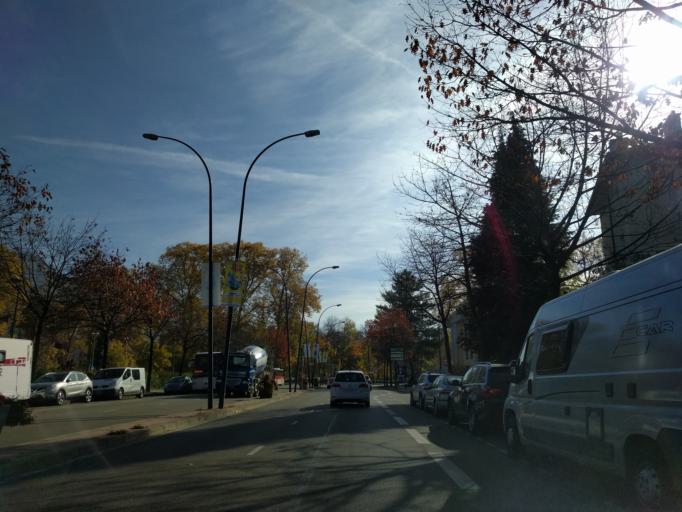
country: FR
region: Rhone-Alpes
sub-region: Departement de la Haute-Savoie
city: Annecy-le-Vieux
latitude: 45.9062
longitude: 6.1417
